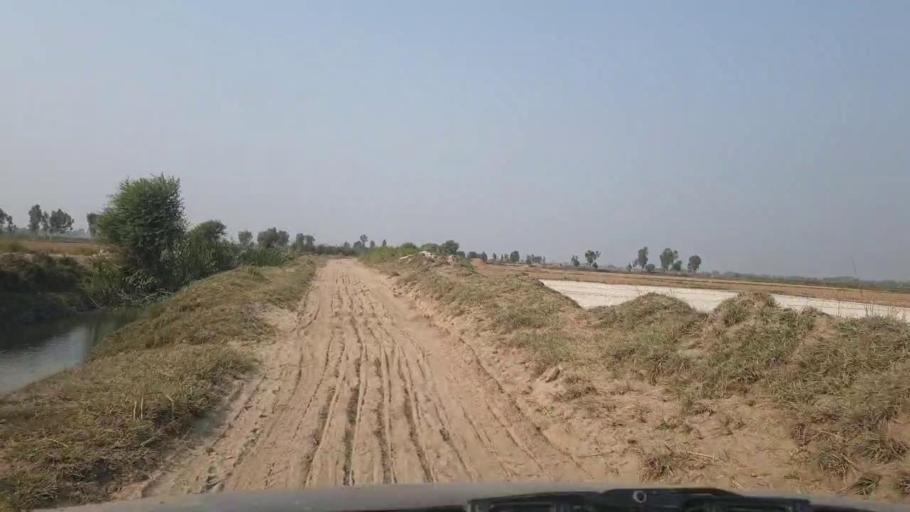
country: PK
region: Sindh
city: Tando Muhammad Khan
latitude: 25.0725
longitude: 68.3556
